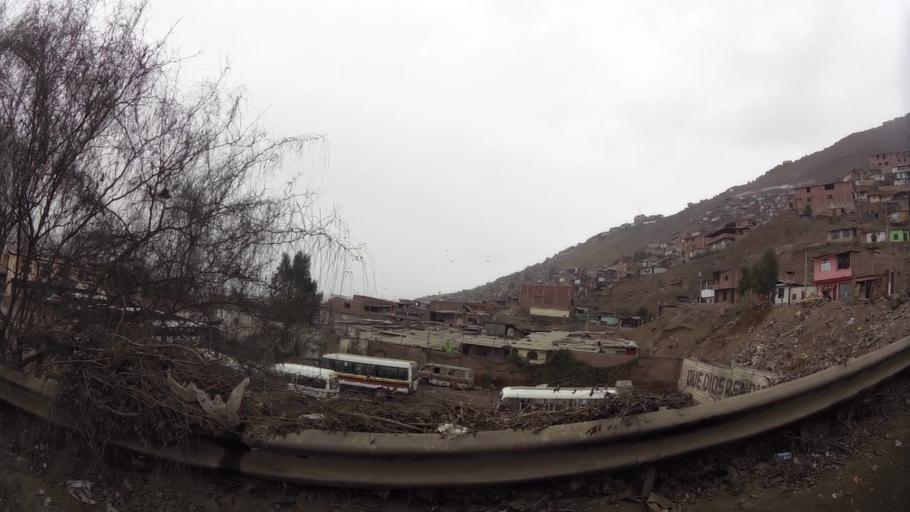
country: PE
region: Lima
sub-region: Lima
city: Surco
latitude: -12.2128
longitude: -76.9143
